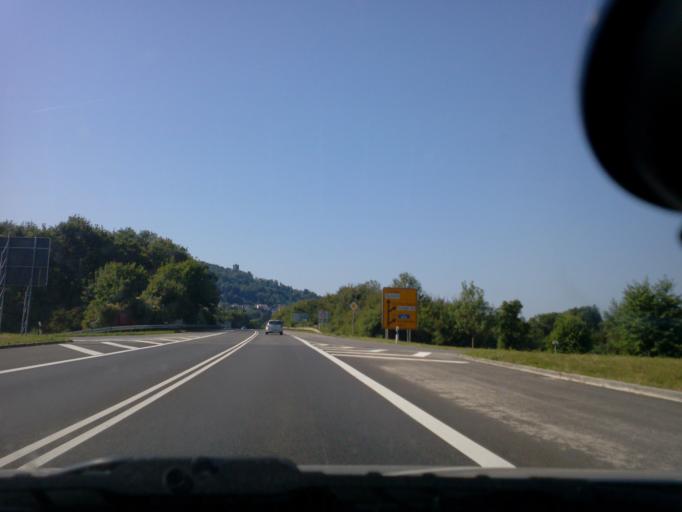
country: DE
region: Baden-Wuerttemberg
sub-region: Karlsruhe Region
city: Weingarten
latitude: 49.0102
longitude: 8.4883
